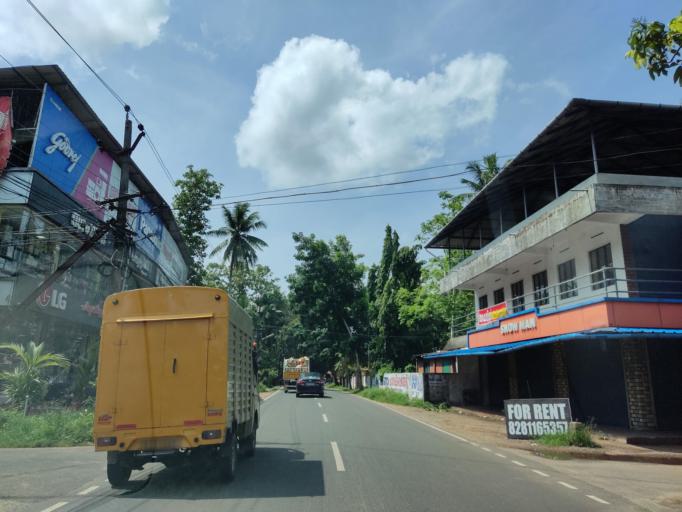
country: IN
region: Kerala
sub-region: Alappuzha
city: Mavelikara
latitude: 9.2748
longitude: 76.5363
